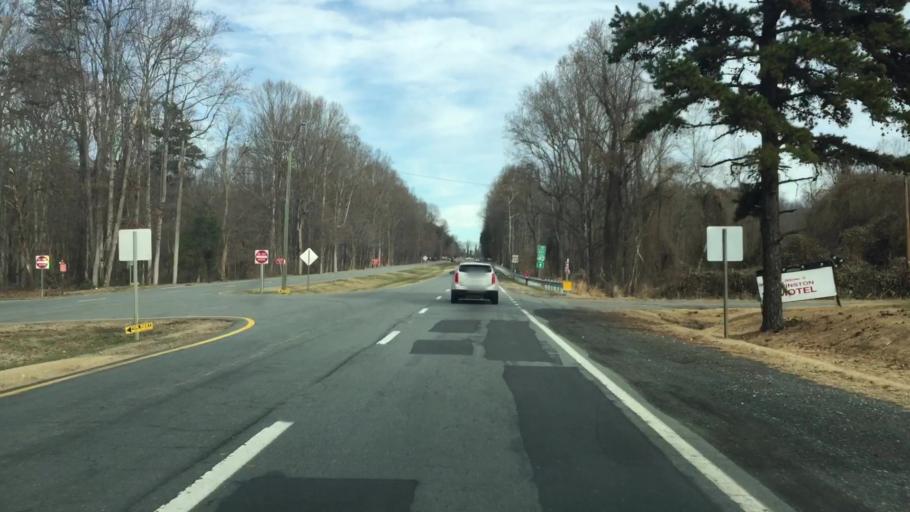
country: US
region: North Carolina
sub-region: Forsyth County
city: Winston-Salem
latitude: 36.1036
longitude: -80.1927
